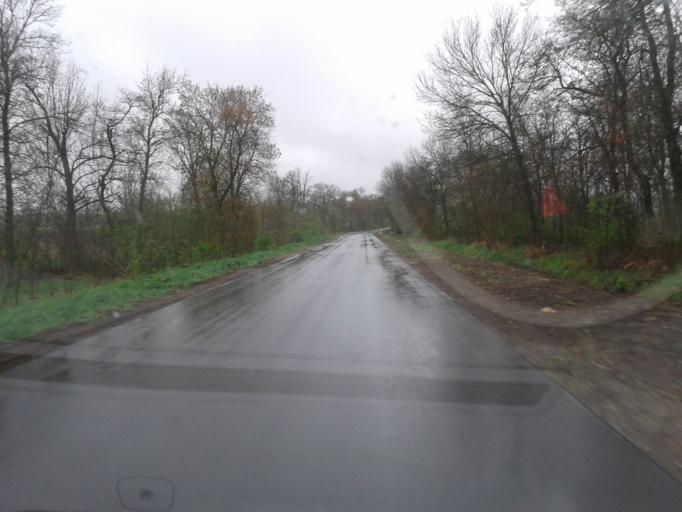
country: PL
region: Lublin Voivodeship
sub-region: Powiat tomaszowski
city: Jarczow
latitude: 50.3637
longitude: 23.5920
